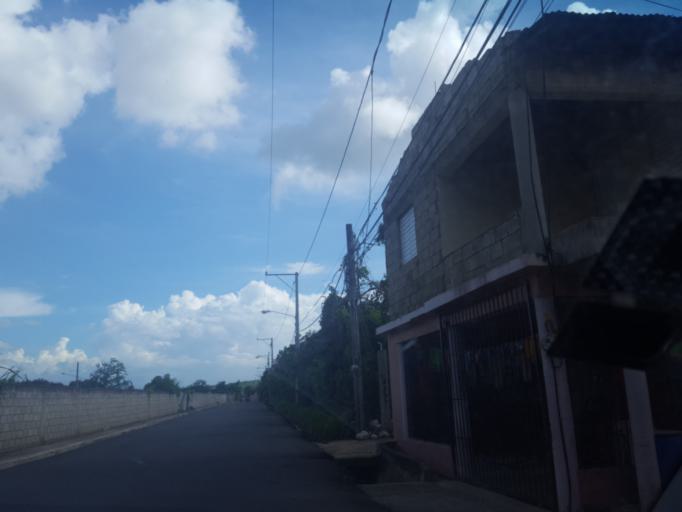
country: DO
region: Santiago
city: Licey al Medio
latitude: 19.3819
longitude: -70.6214
